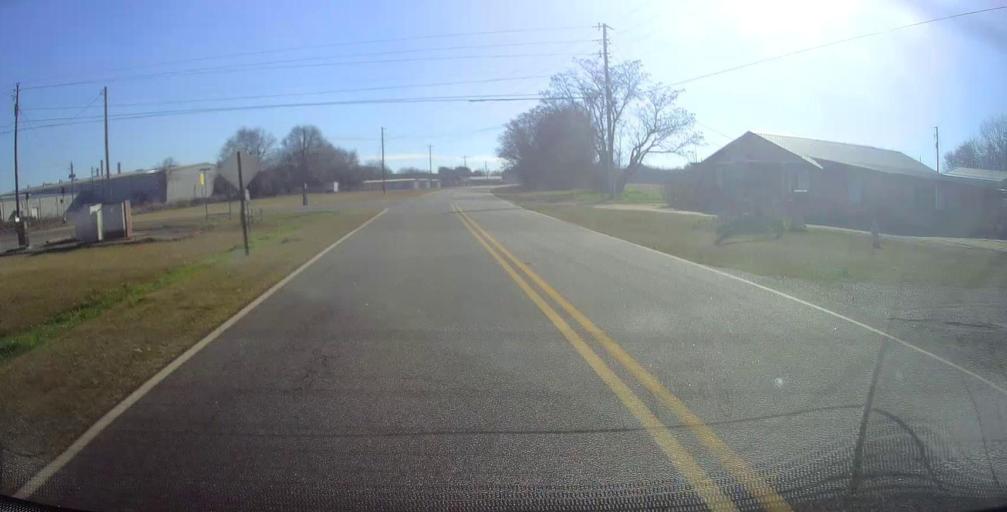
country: US
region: Georgia
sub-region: Sumter County
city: Americus
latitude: 32.1113
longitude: -84.2009
